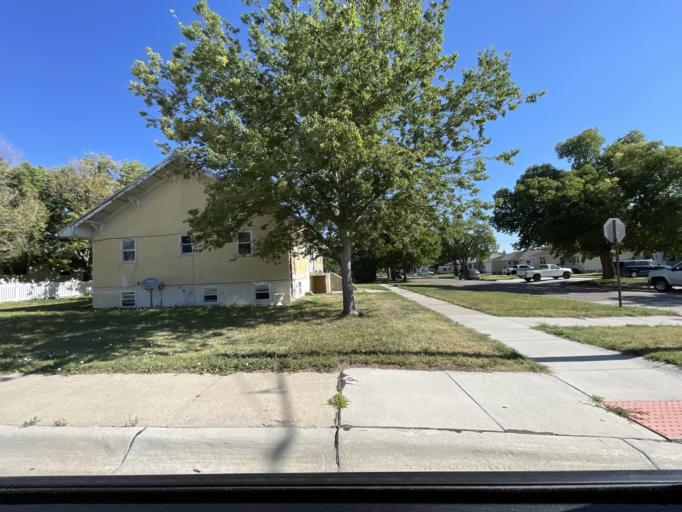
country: US
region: Nebraska
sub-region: Red Willow County
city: McCook
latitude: 40.2046
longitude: -100.6190
